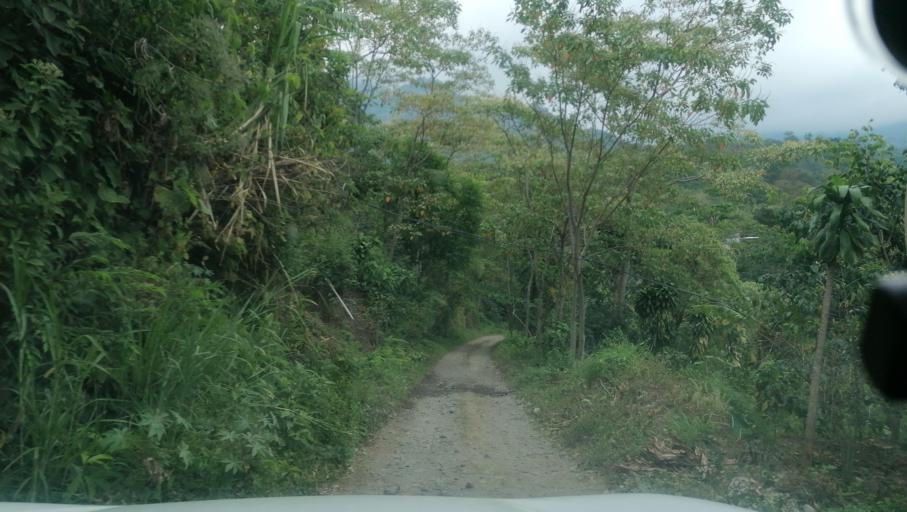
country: MX
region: Chiapas
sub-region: Cacahoatan
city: Benito Juarez
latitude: 15.1683
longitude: -92.1686
